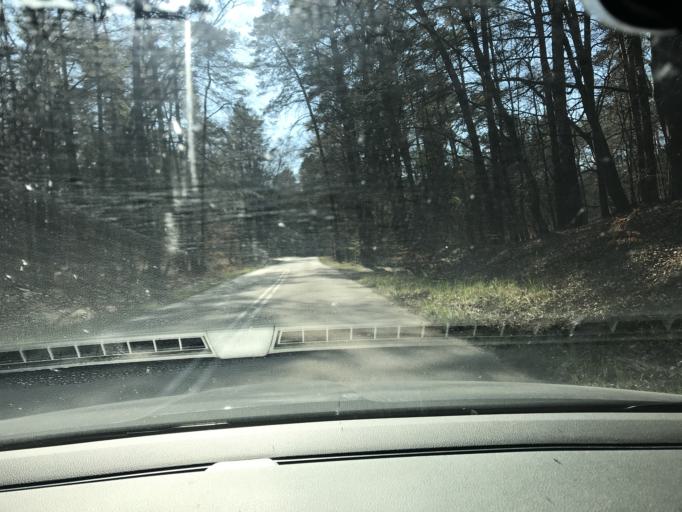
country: PL
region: Pomeranian Voivodeship
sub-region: Powiat nowodworski
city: Krynica Morska
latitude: 54.3632
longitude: 19.3615
